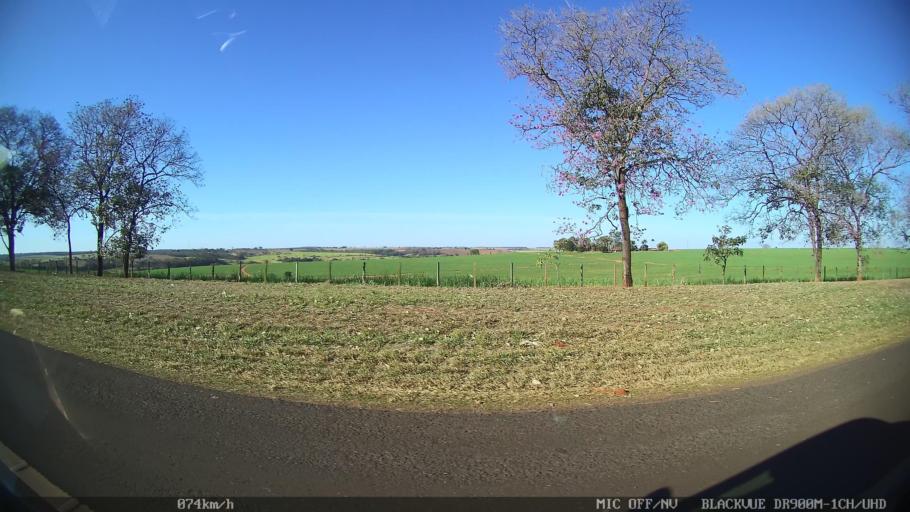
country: BR
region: Sao Paulo
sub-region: Olimpia
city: Olimpia
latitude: -20.7022
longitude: -48.9133
